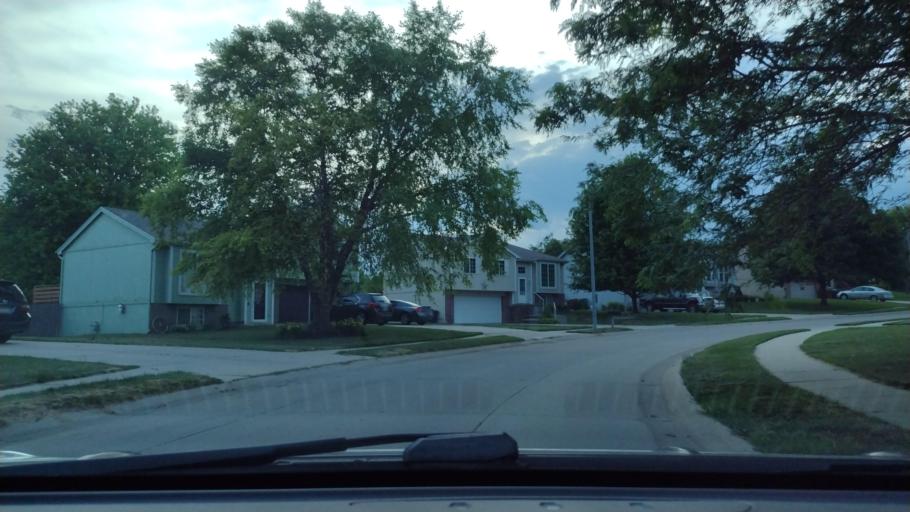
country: US
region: Nebraska
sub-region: Sarpy County
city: Offutt Air Force Base
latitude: 41.1514
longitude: -95.9422
